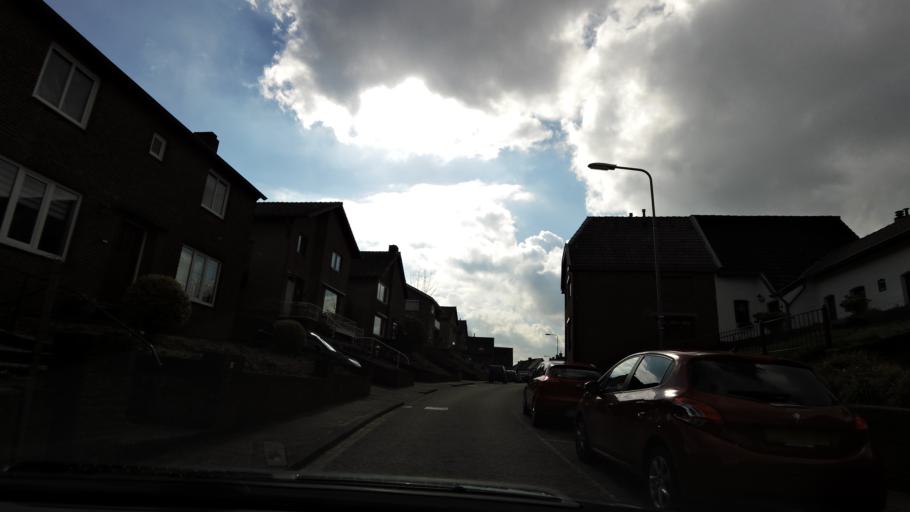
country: NL
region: Limburg
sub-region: Gemeente Voerendaal
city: Ubachsberg
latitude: 50.7943
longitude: 5.9264
